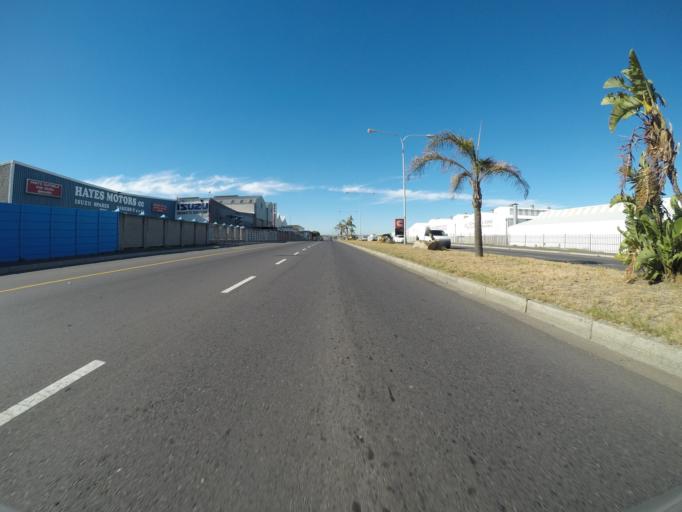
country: ZA
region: Western Cape
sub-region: City of Cape Town
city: Kraaifontein
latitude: -33.9013
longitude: 18.6695
